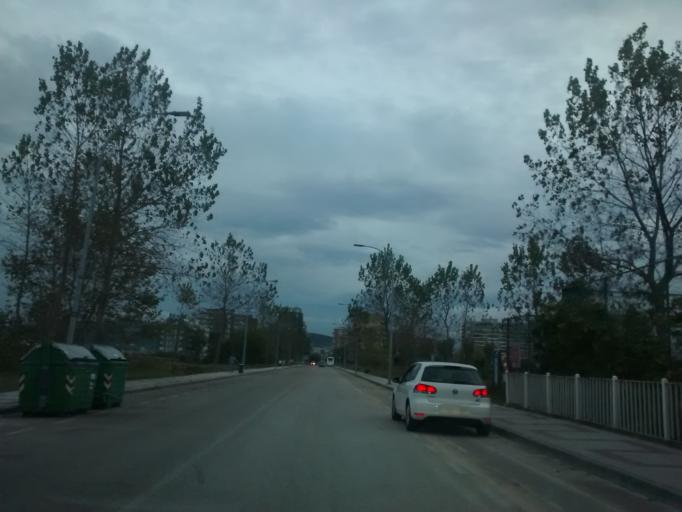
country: ES
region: Cantabria
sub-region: Provincia de Cantabria
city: Santona
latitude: 43.4316
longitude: -3.4498
